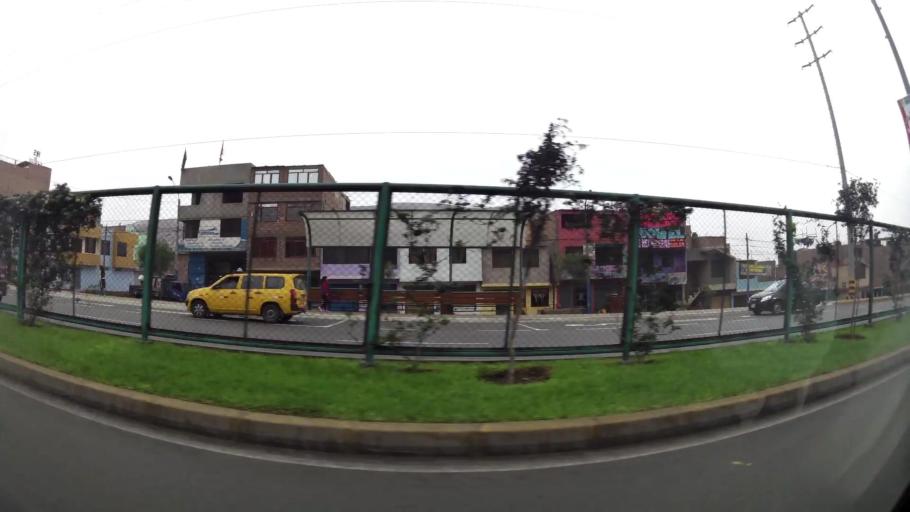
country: PE
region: Lima
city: Ventanilla
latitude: -11.8954
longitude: -77.1267
